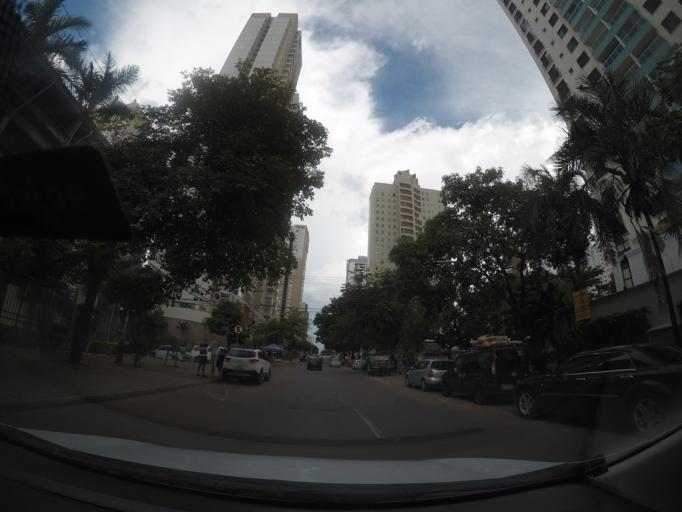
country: BR
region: Goias
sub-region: Goiania
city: Goiania
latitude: -16.7193
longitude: -49.2682
